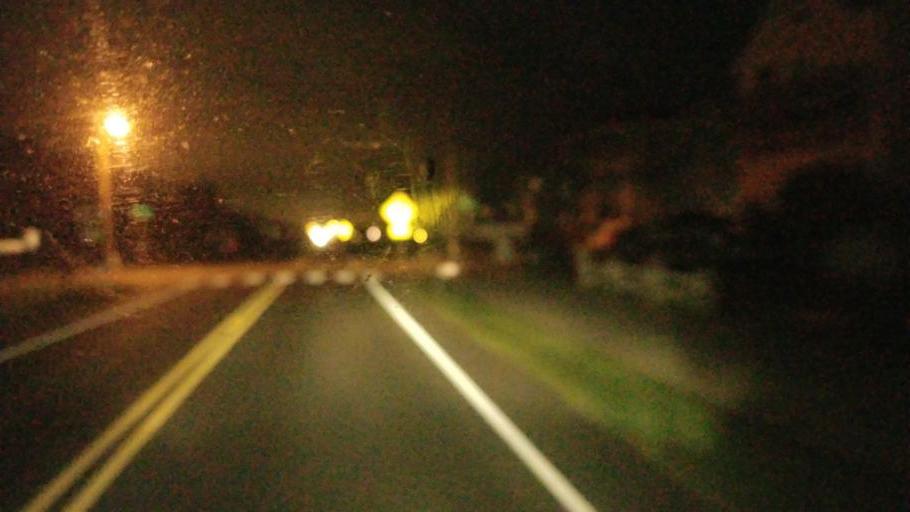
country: US
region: North Carolina
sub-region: Dare County
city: Nags Head
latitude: 35.9890
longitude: -75.6424
